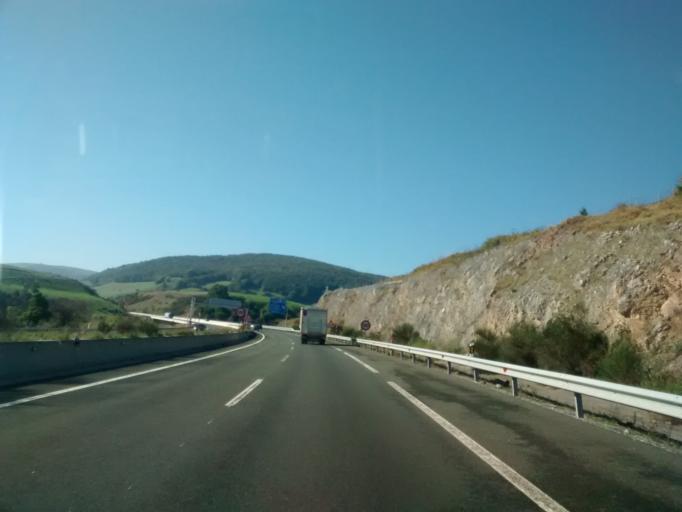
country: ES
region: Cantabria
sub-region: Provincia de Cantabria
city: Pesquera
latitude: 43.0839
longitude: -4.0835
